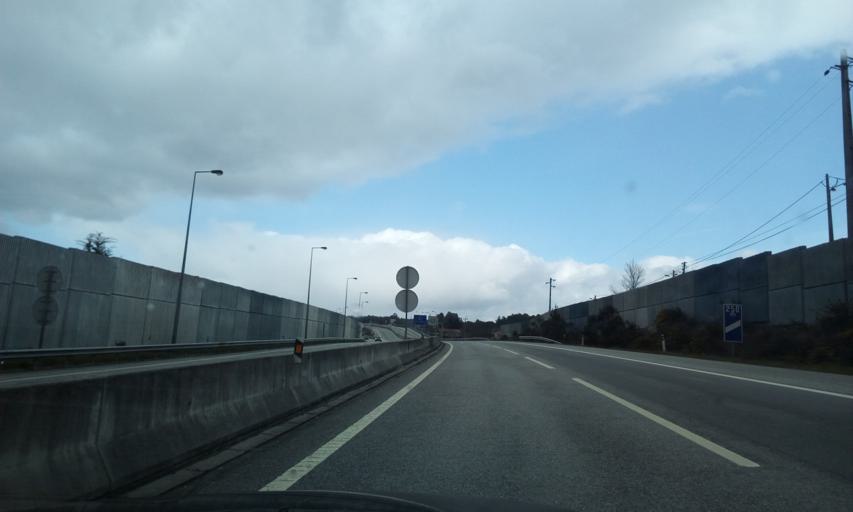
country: PT
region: Viseu
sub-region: Viseu
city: Rio de Loba
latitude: 40.6486
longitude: -7.8607
